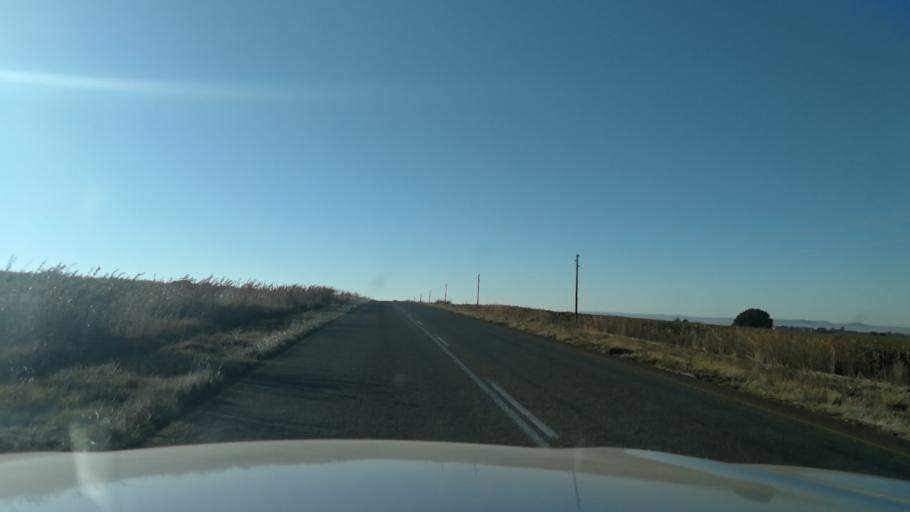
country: ZA
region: North-West
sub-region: Bojanala Platinum District Municipality
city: Koster
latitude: -25.9161
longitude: 27.0701
